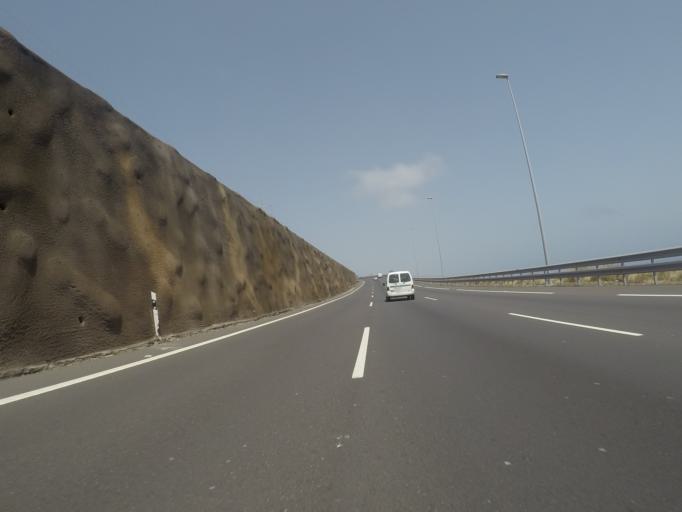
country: ES
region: Canary Islands
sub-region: Provincia de Santa Cruz de Tenerife
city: Santa Cruz de Tenerife
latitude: 28.4373
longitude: -16.2808
